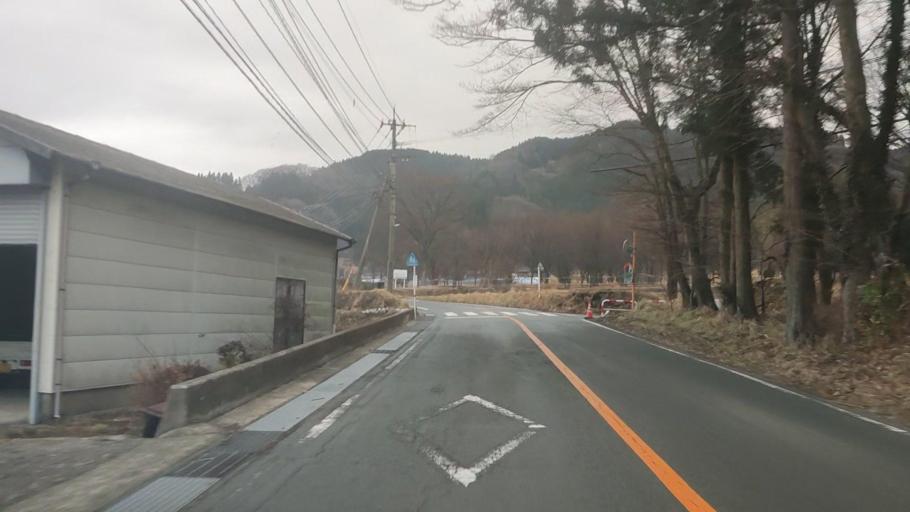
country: JP
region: Kumamoto
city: Aso
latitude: 32.8627
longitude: 131.1662
